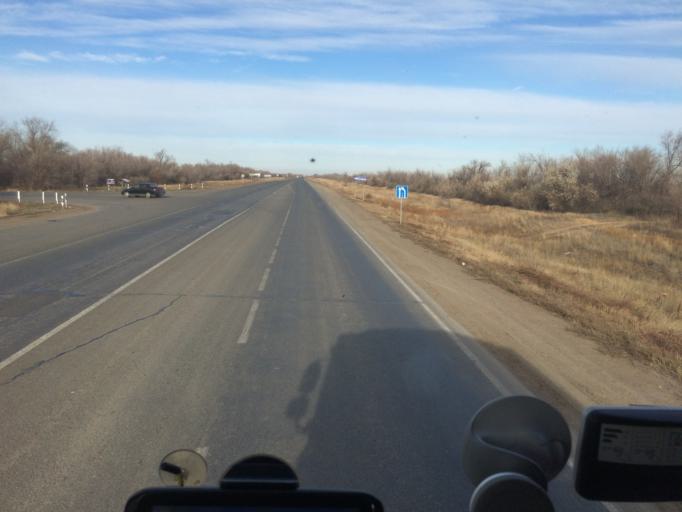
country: KZ
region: Batys Qazaqstan
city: Oral
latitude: 51.3112
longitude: 51.3512
